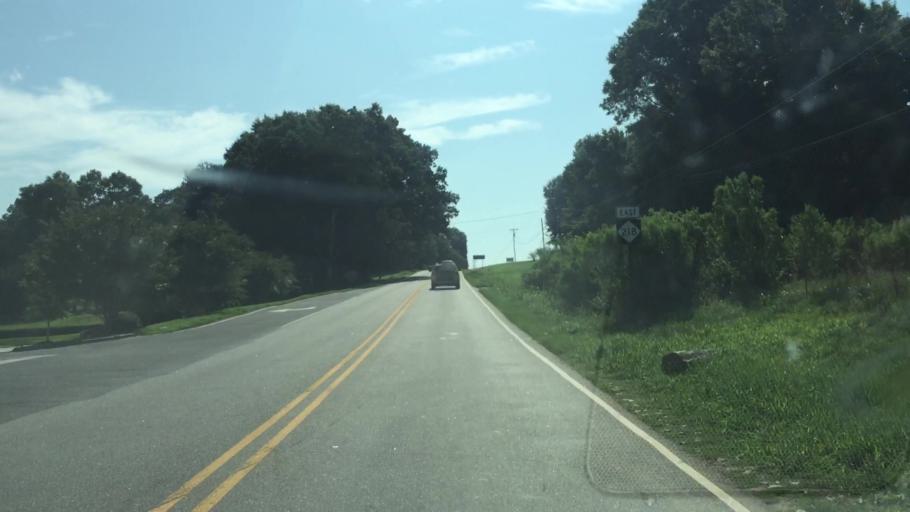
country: US
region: North Carolina
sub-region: Union County
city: Fairview
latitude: 35.1382
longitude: -80.5368
